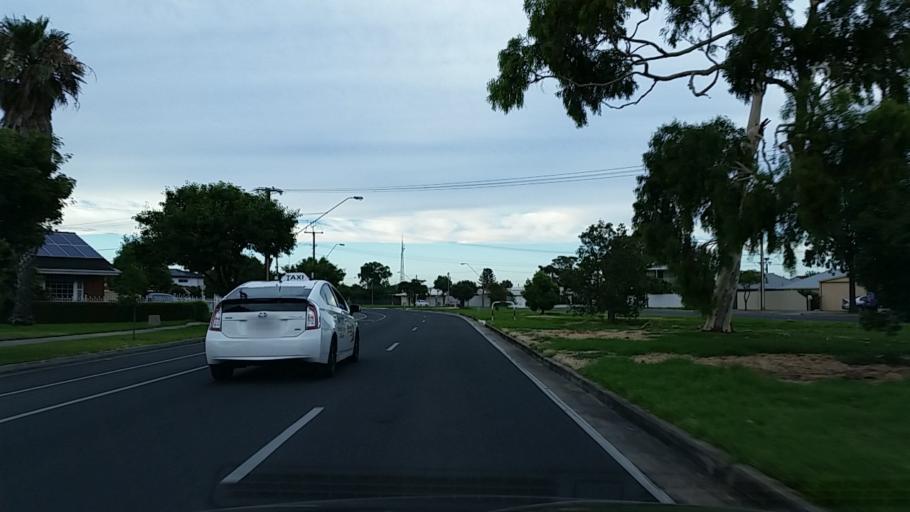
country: AU
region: South Australia
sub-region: City of West Torrens
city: Plympton
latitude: -34.9280
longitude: 138.5435
